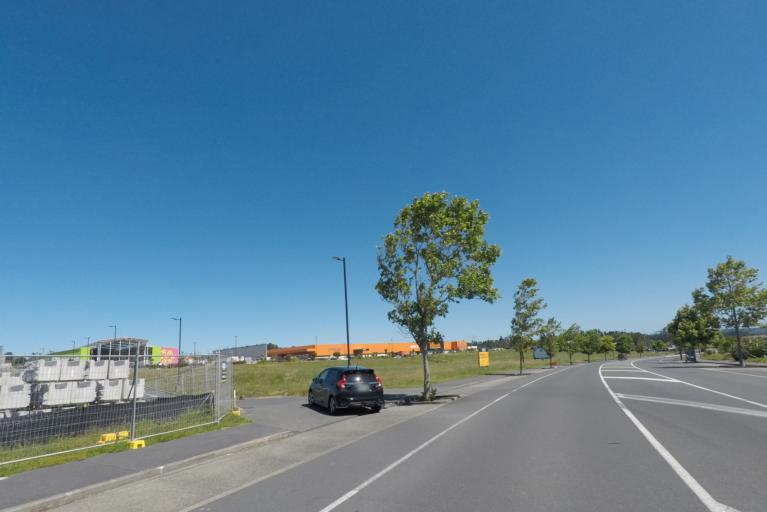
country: NZ
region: Auckland
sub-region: Auckland
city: Rosebank
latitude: -36.8108
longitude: 174.6067
